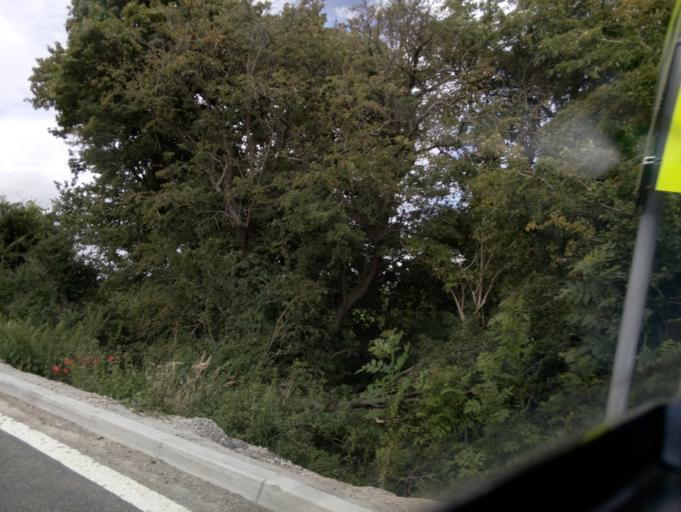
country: GB
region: England
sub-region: Somerset
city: Yeovil
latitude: 50.9127
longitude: -2.6236
